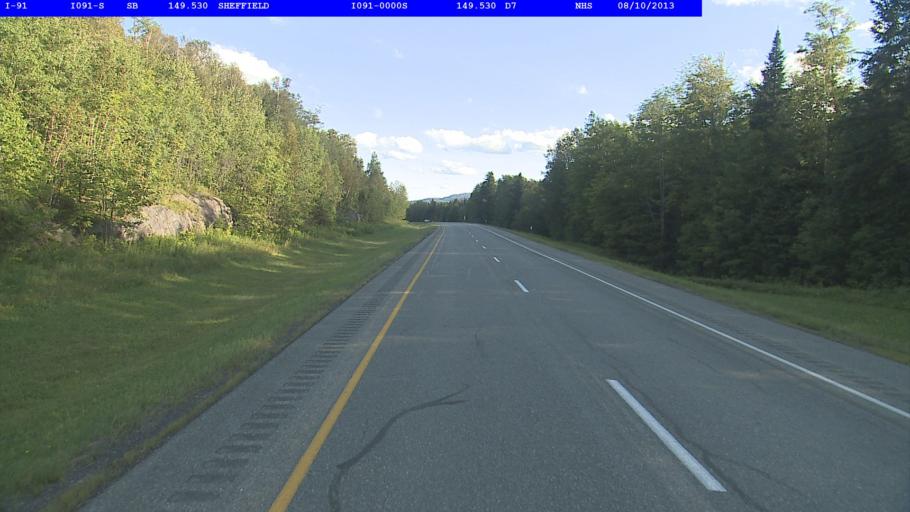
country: US
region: Vermont
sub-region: Caledonia County
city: Lyndonville
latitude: 44.6579
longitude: -72.1349
